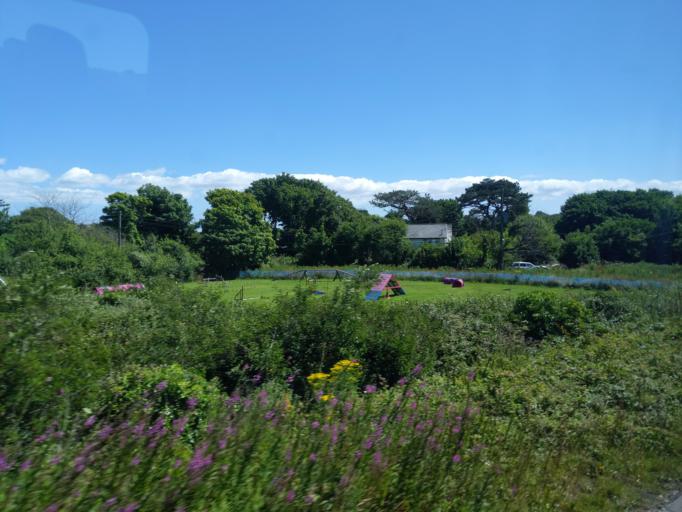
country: GB
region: England
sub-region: Cornwall
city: St. Day
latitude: 50.2564
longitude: -5.1926
